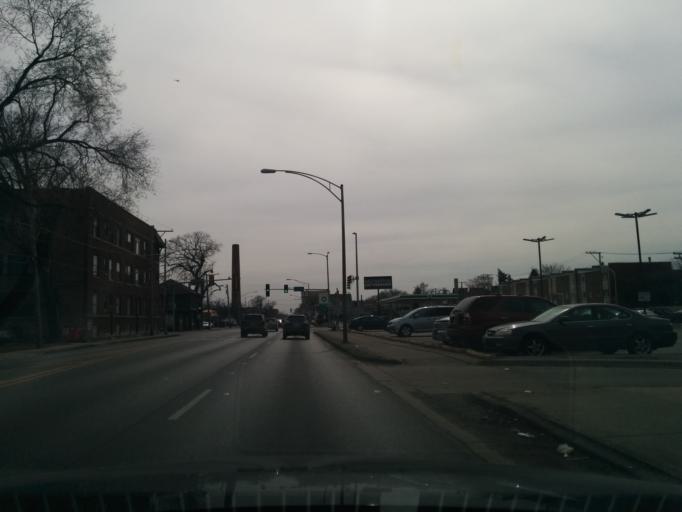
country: US
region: Illinois
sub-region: Cook County
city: Forest Park
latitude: 41.8822
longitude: -87.8049
